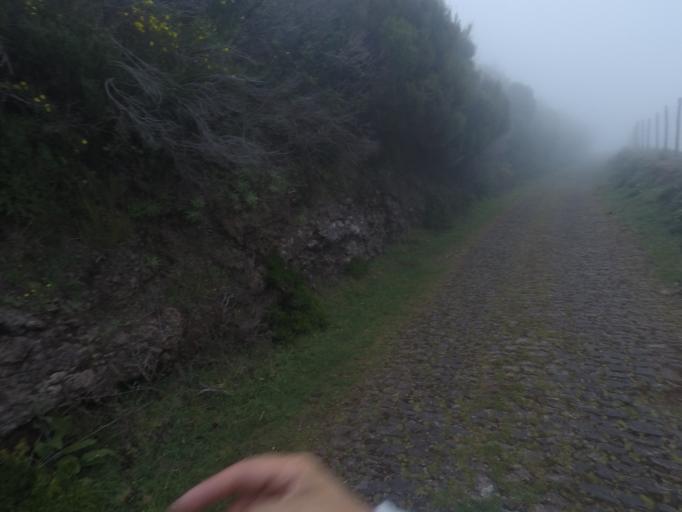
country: PT
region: Madeira
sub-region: Calheta
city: Arco da Calheta
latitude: 32.7336
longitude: -17.0966
